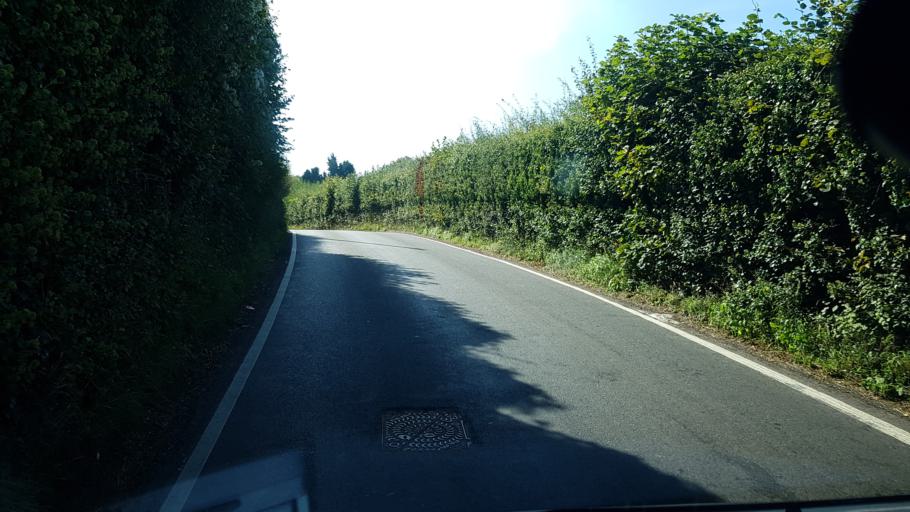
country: GB
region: England
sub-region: Kent
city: Yalding
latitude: 51.2413
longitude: 0.4661
